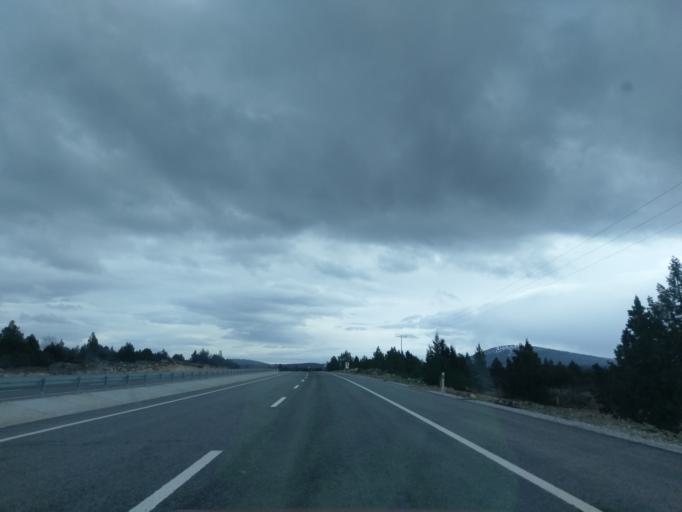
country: TR
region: Kuetahya
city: Cavdarhisar
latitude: 39.2231
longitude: 29.7313
